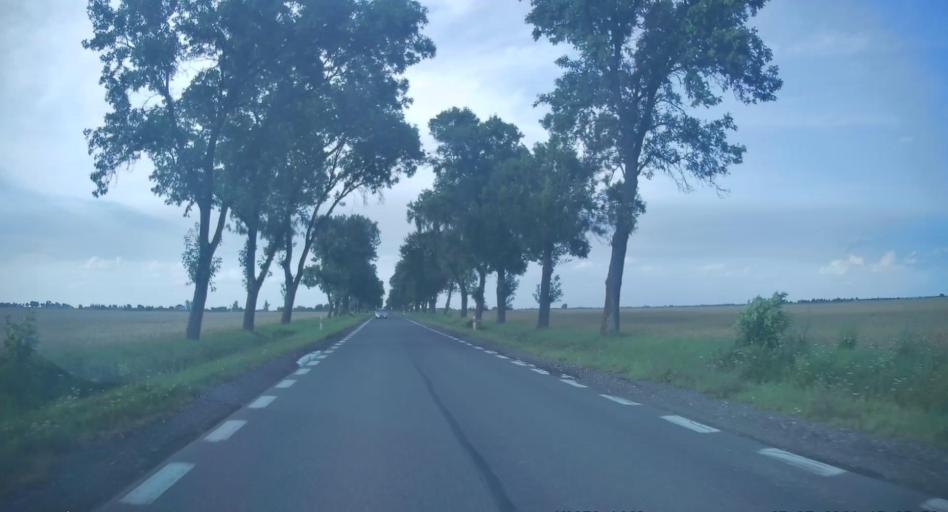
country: PL
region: Lodz Voivodeship
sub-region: Powiat tomaszowski
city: Rzeczyca
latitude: 51.6199
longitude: 20.2930
